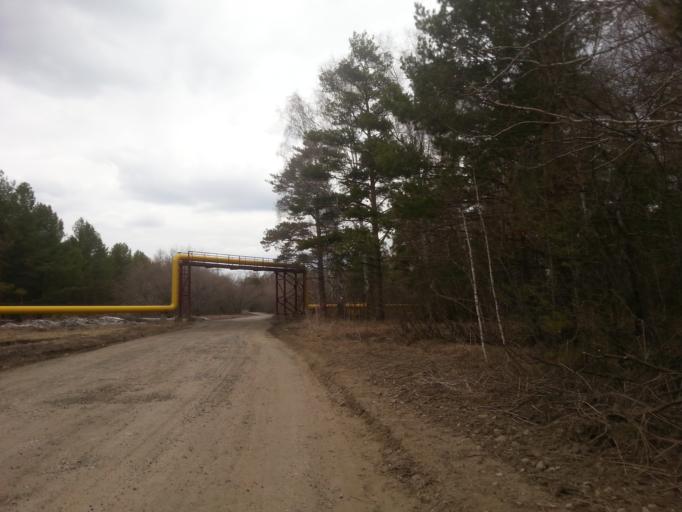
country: RU
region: Altai Krai
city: Yuzhnyy
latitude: 53.2851
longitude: 83.7311
